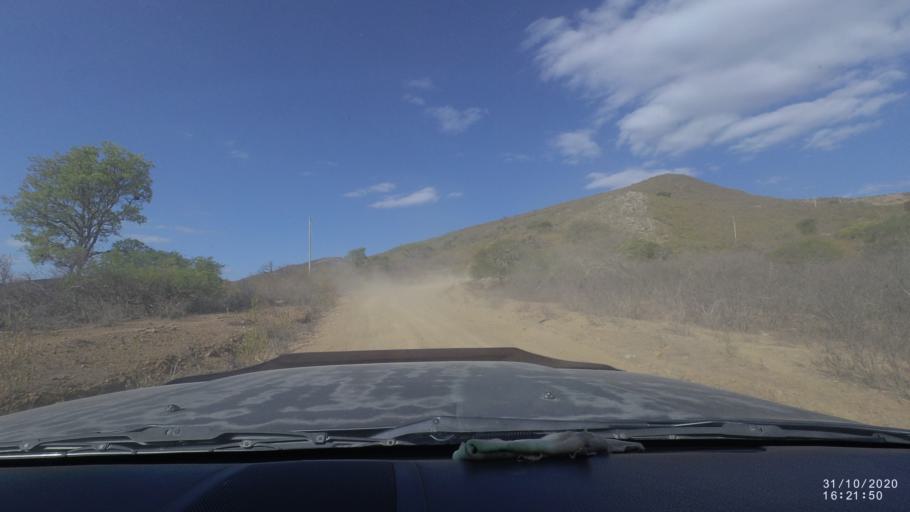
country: BO
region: Chuquisaca
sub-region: Provincia Zudanez
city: Mojocoya
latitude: -18.3989
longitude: -64.5952
